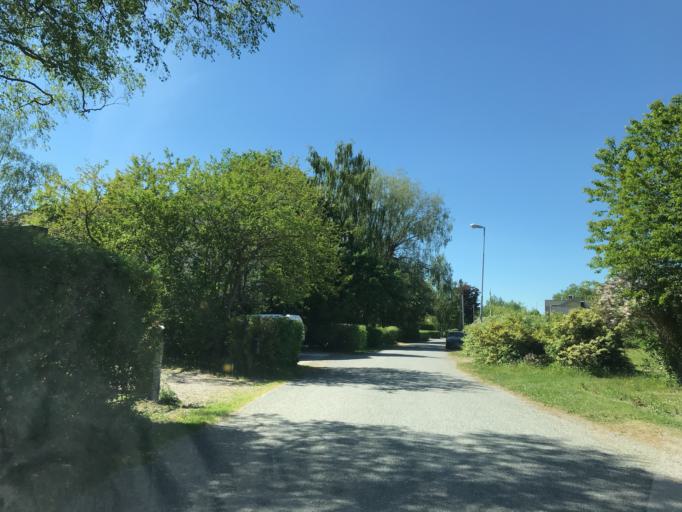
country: SE
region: Stockholm
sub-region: Sollentuna Kommun
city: Sollentuna
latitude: 59.4190
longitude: 17.9666
